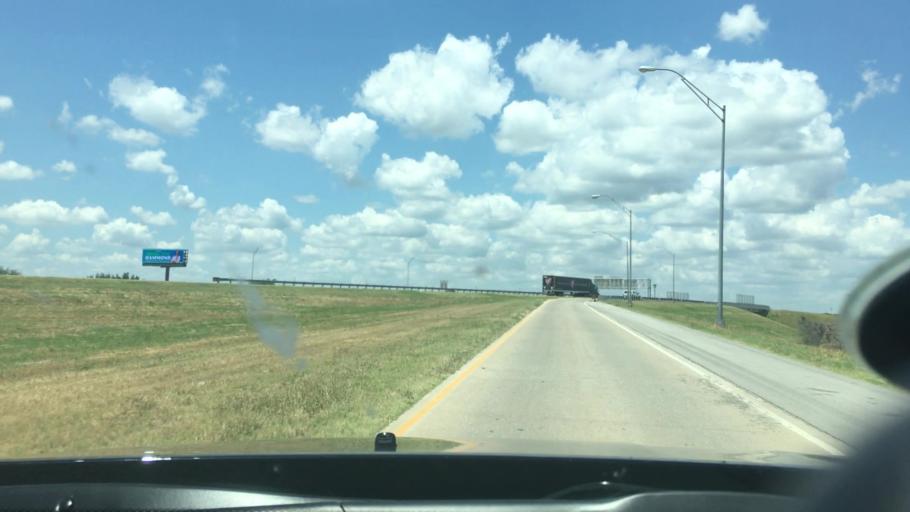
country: US
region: Oklahoma
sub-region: Carter County
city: Ardmore
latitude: 34.1750
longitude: -97.1669
